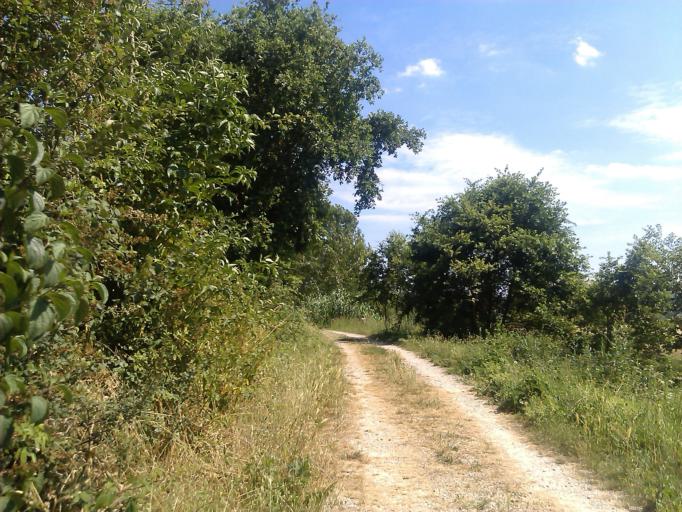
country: IT
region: Tuscany
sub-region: Provincia di Siena
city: Chiusi
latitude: 43.0567
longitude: 11.9360
